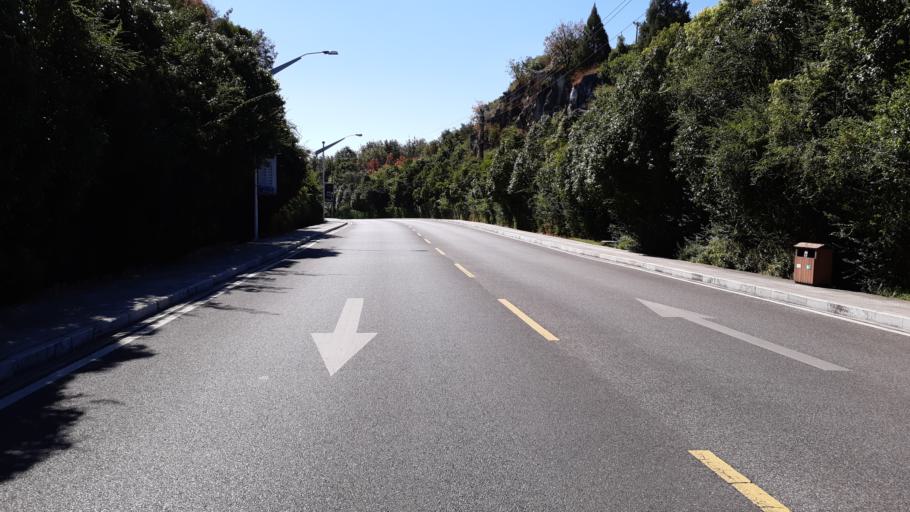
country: CN
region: Yunnan
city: Shilin
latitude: 24.8295
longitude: 103.3248
